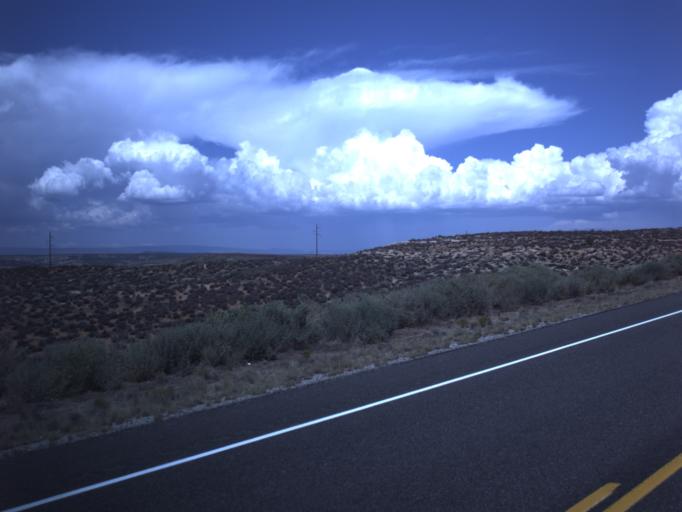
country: US
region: Utah
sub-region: San Juan County
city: Blanding
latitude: 37.3829
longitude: -109.5019
